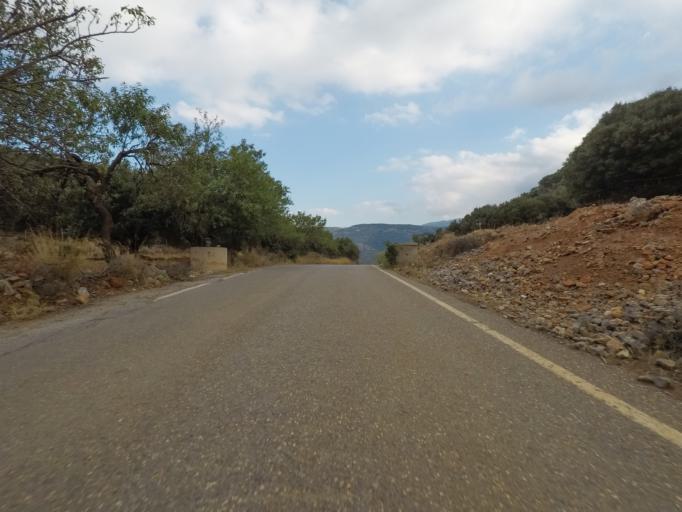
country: GR
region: Crete
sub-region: Nomos Lasithiou
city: Kritsa
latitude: 35.1691
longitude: 25.6546
